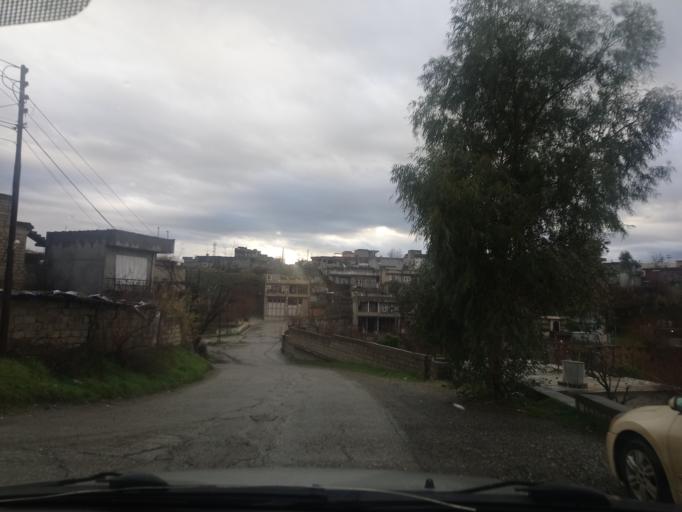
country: IQ
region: As Sulaymaniyah
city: Qeladize
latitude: 36.1819
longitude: 45.1221
